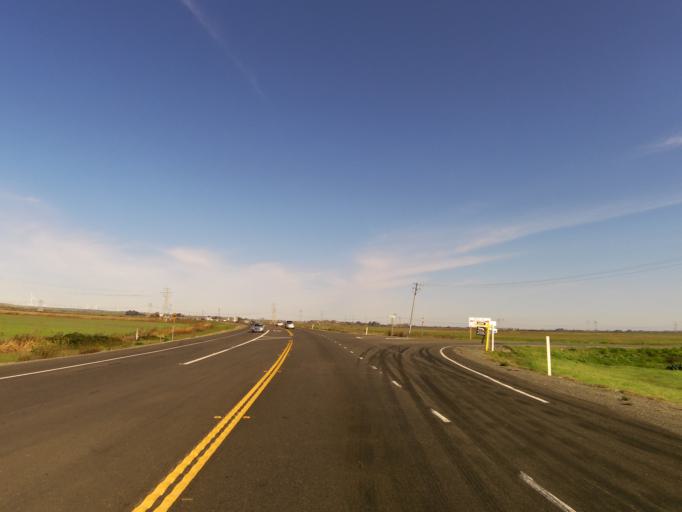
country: US
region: California
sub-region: Contra Costa County
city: Oakley
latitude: 38.0580
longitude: -121.7391
